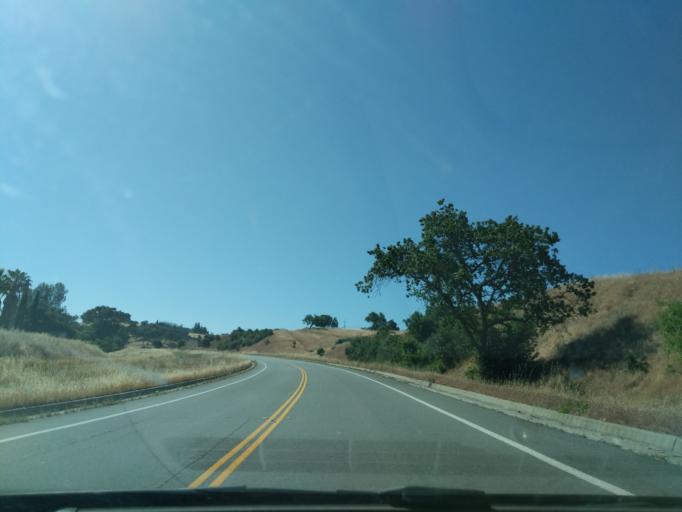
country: US
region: California
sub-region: Santa Clara County
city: San Martin
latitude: 37.0900
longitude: -121.6384
